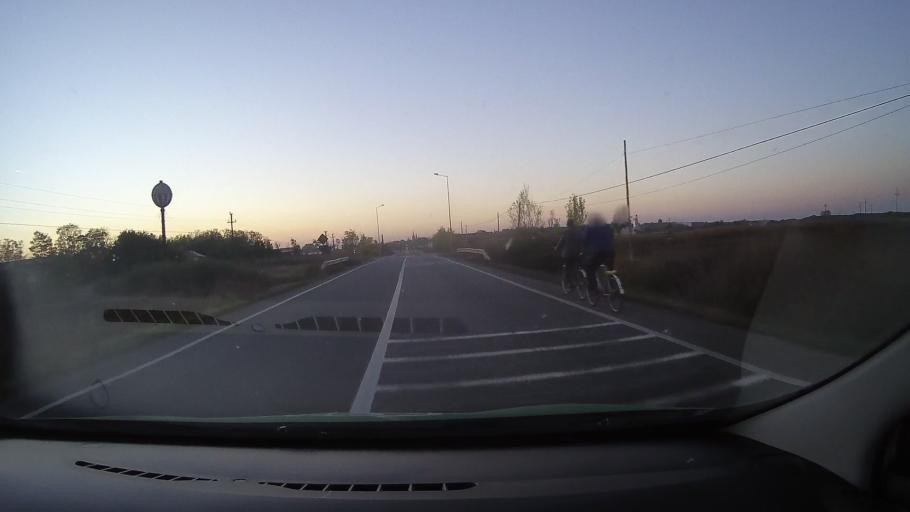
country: RO
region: Bihor
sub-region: Comuna Tarcea
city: Tarcea
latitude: 47.4534
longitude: 22.1806
